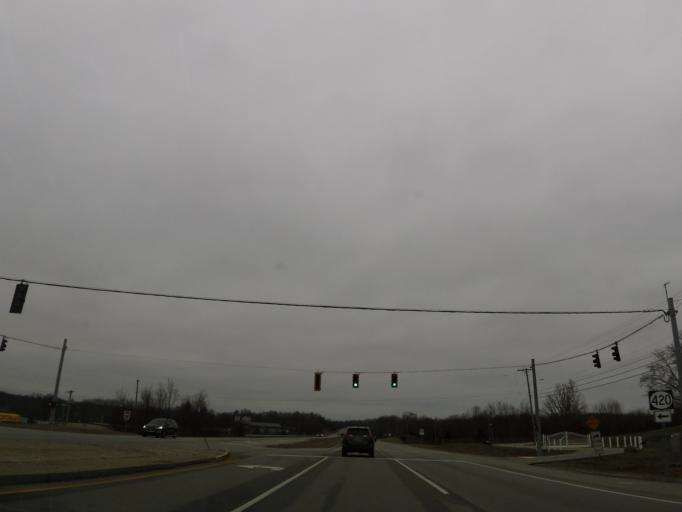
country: US
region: Kentucky
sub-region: Franklin County
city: Frankfort
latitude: 38.1485
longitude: -84.8974
